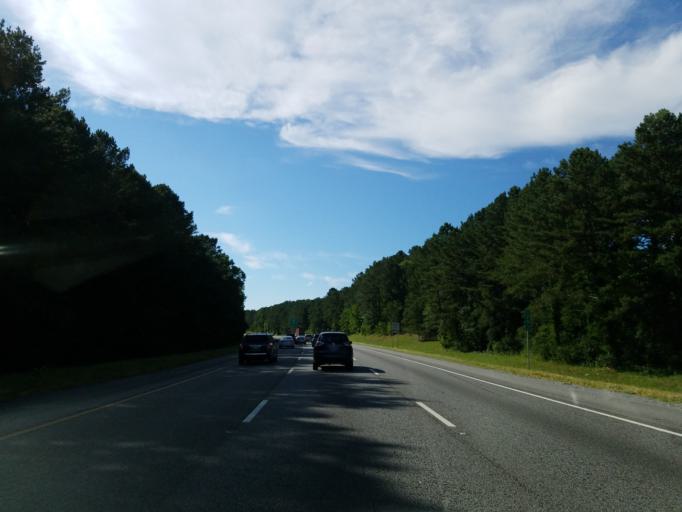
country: US
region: Georgia
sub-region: Bartow County
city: Cartersville
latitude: 34.2324
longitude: -84.7542
